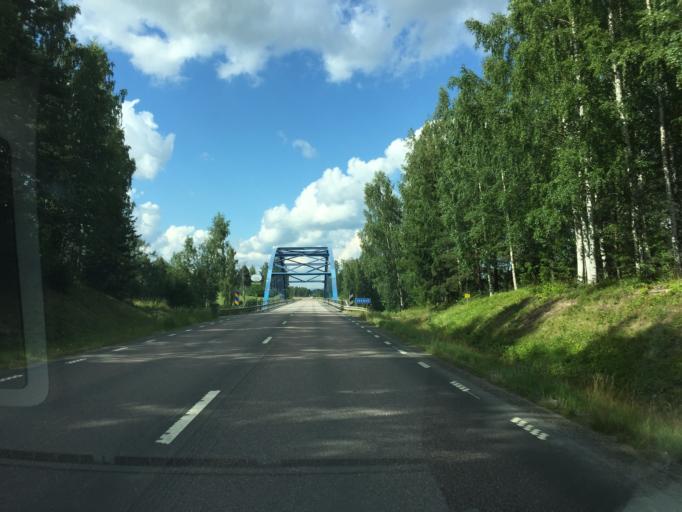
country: SE
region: Gaevleborg
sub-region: Bollnas Kommun
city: Bollnas
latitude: 61.3148
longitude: 16.4407
